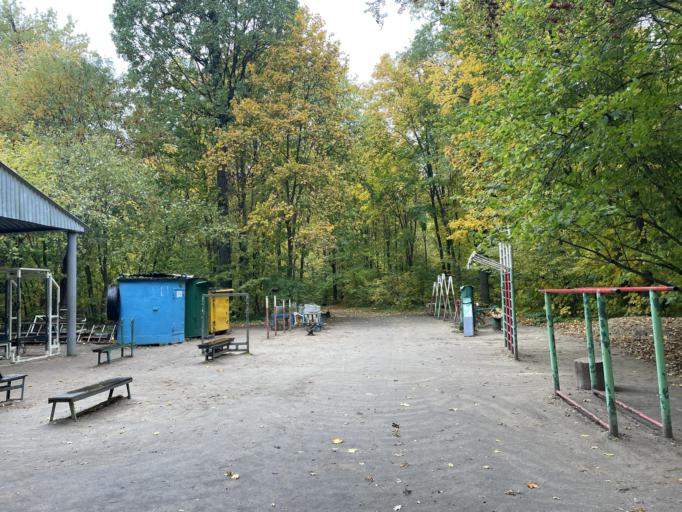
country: RU
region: Chuvashia
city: Novocheboksarsk
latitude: 56.1195
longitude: 47.4664
